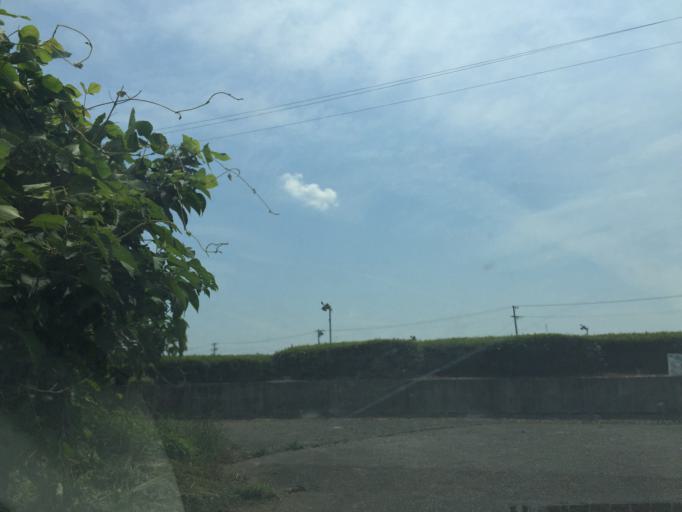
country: JP
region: Shizuoka
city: Mori
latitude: 34.7956
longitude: 137.9502
